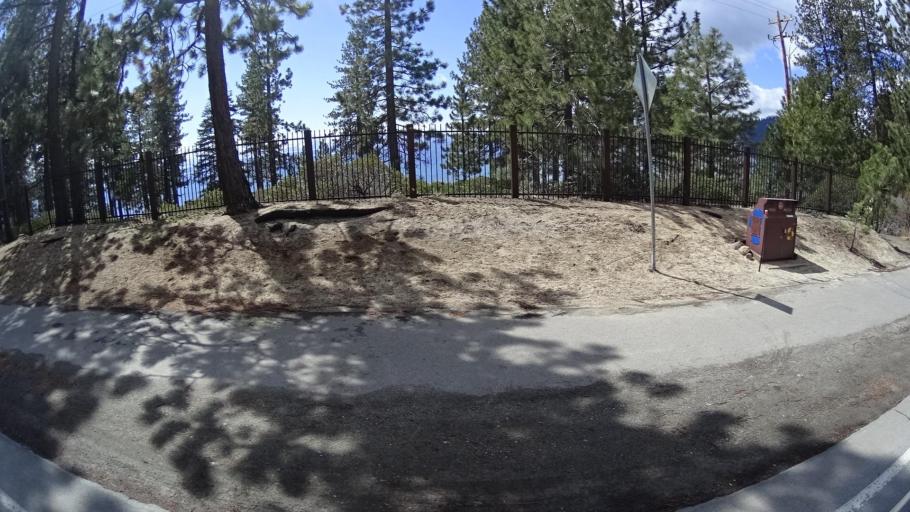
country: US
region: Nevada
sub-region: Washoe County
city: Incline Village
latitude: 39.2476
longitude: -119.9702
